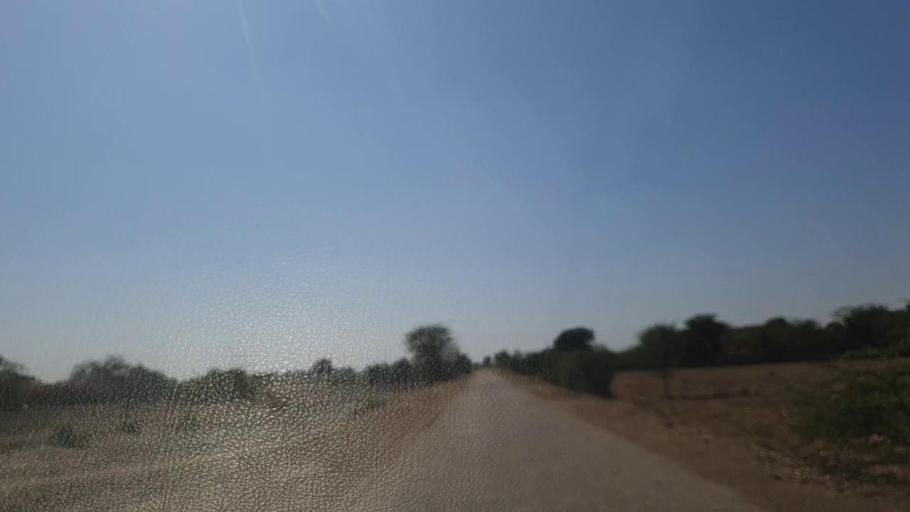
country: PK
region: Sindh
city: Naukot
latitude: 25.0586
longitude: 69.3862
